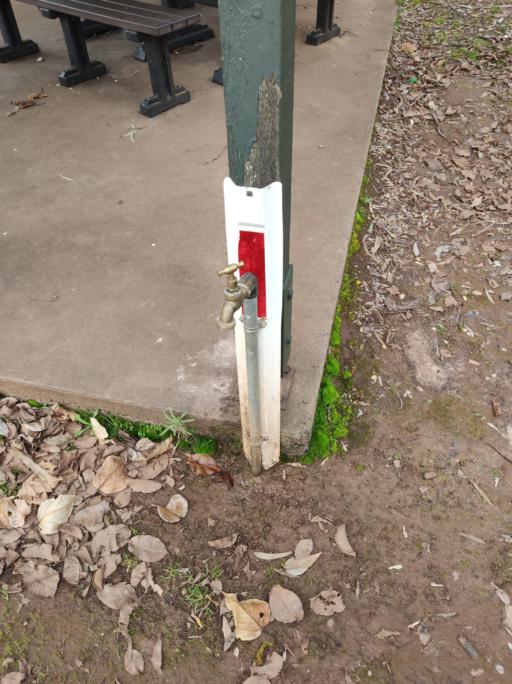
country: AU
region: New South Wales
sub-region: Orange Municipality
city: Orange
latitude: -33.3042
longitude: 149.0299
